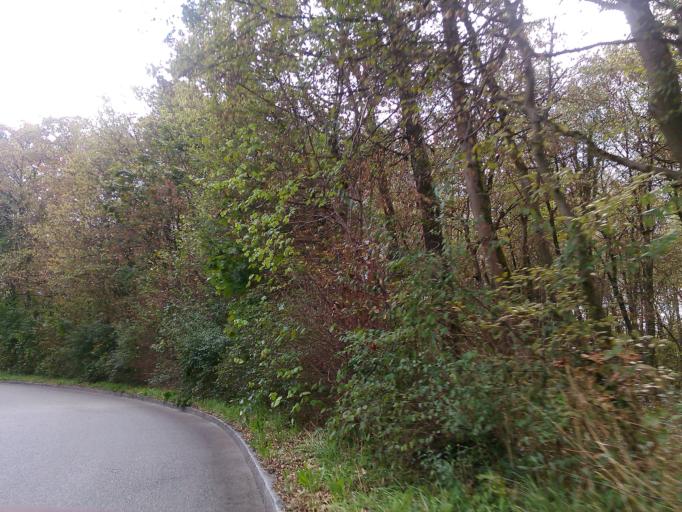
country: DE
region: Bavaria
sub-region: Upper Bavaria
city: Planegg
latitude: 48.1103
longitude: 11.4159
